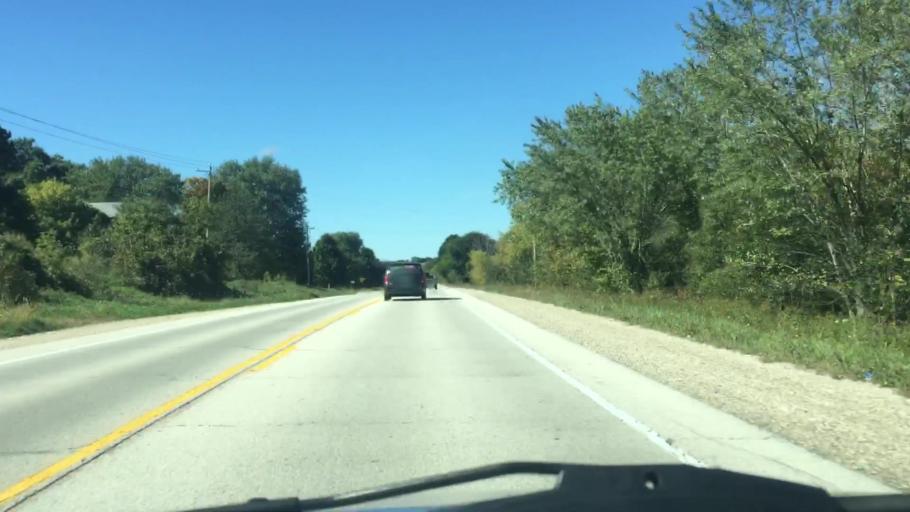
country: US
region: Wisconsin
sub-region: Waukesha County
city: Wales
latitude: 43.0201
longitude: -88.3304
